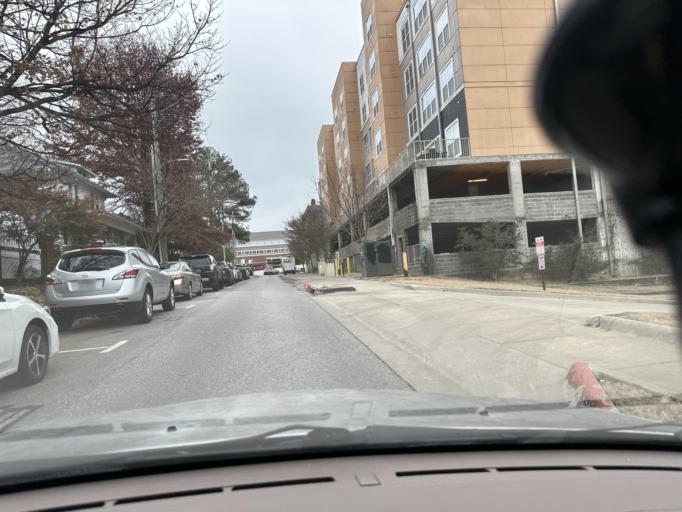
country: US
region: Arkansas
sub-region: Washington County
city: Fayetteville
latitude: 36.0675
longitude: -94.1620
